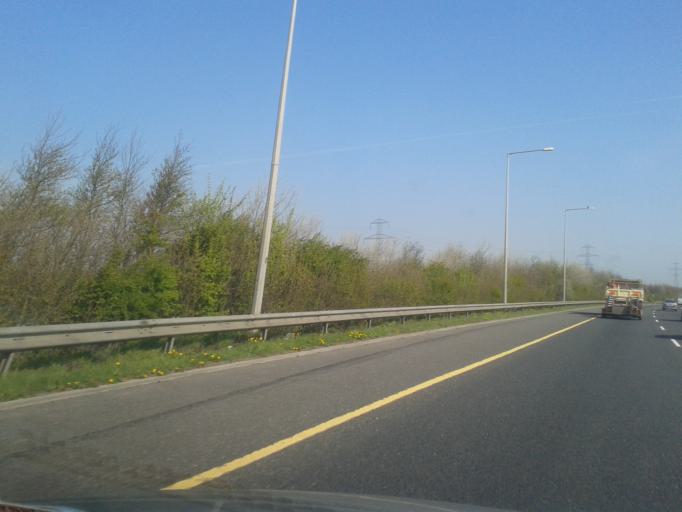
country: IE
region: Leinster
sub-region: Fingal County
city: Swords
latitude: 53.4850
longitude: -6.2069
